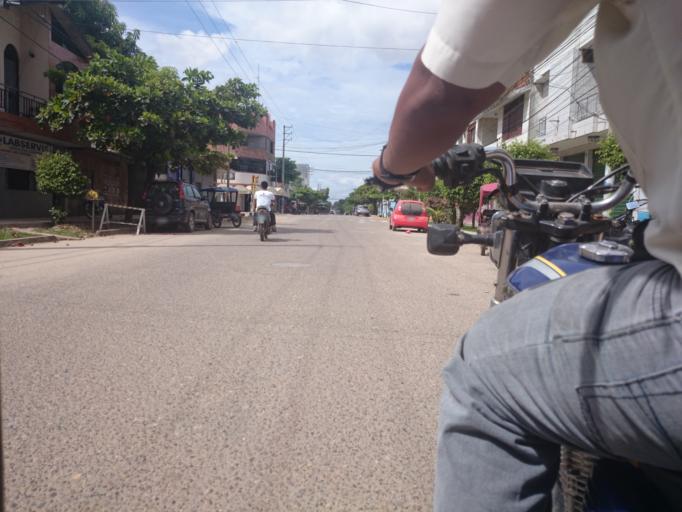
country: PE
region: Ucayali
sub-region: Provincia de Coronel Portillo
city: Pucallpa
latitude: -8.3814
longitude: -74.5329
